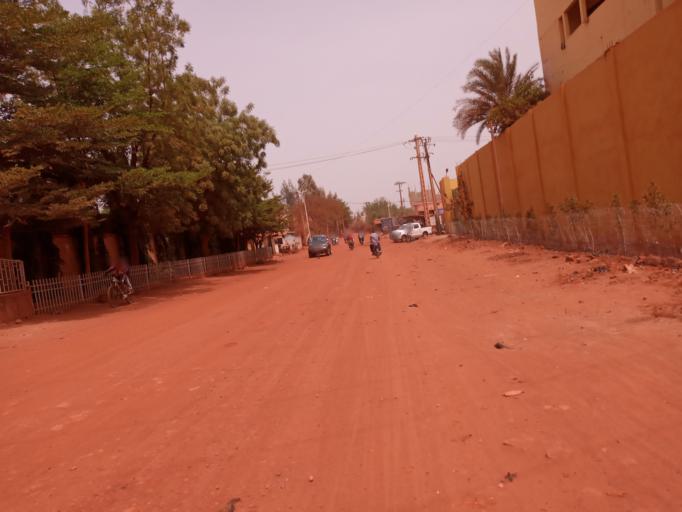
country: ML
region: Bamako
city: Bamako
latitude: 12.6710
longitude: -7.9108
